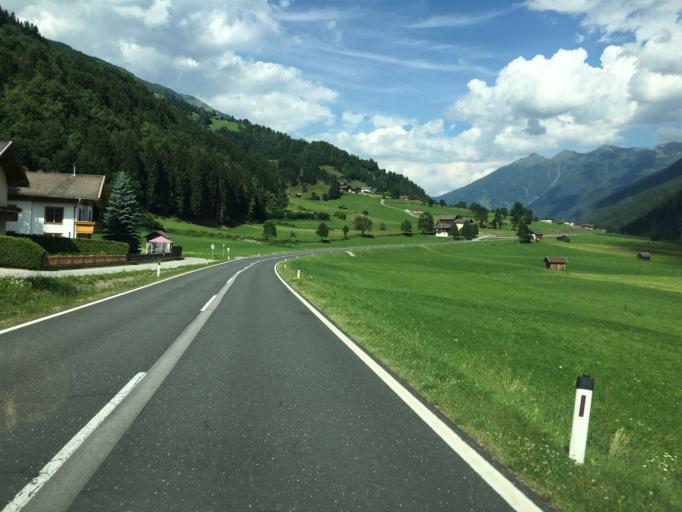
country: AT
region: Carinthia
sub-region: Politischer Bezirk Spittal an der Drau
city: Rangersdorf
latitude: 46.8695
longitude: 12.9768
